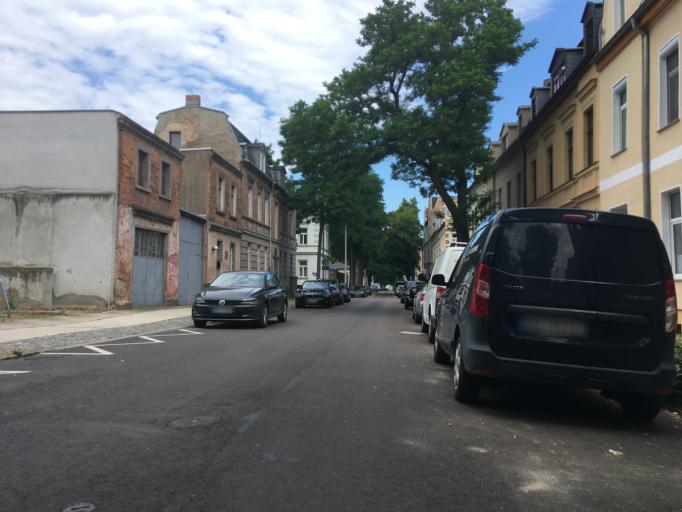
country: DE
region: Saxony-Anhalt
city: Bernburg
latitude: 51.7915
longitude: 11.7497
